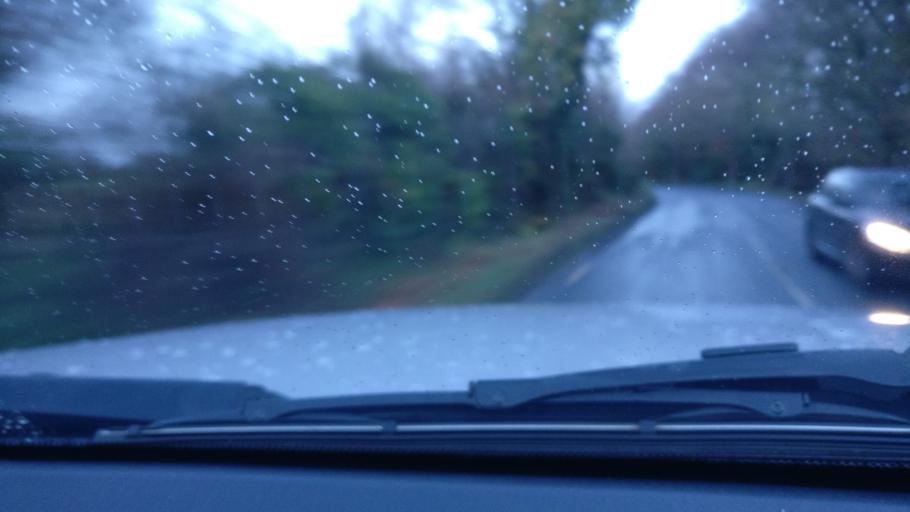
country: IE
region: Connaught
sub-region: County Galway
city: Ballinasloe
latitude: 53.2783
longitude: -8.2422
